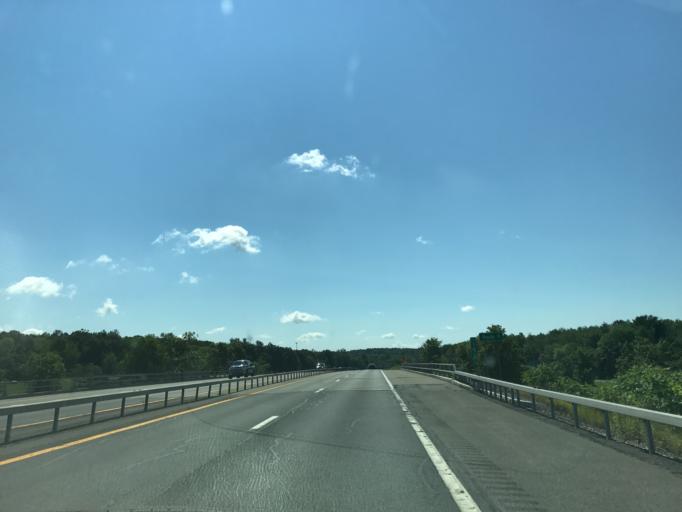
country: US
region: New York
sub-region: Columbia County
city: Niverville
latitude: 42.4900
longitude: -73.6791
